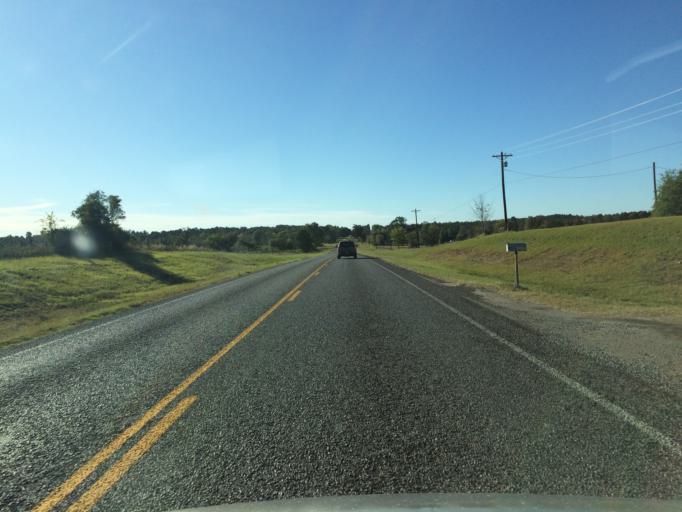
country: US
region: Texas
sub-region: Wood County
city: Hawkins
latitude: 32.6473
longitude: -95.2211
